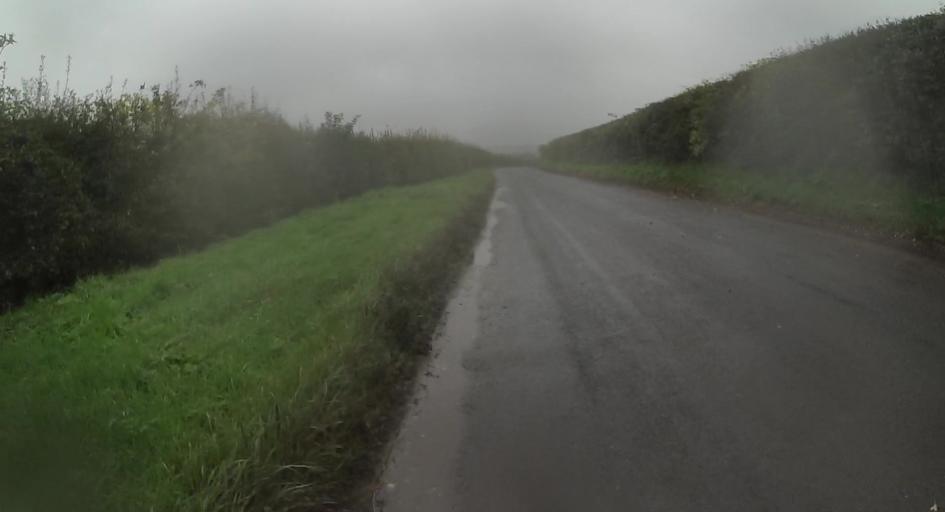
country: GB
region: England
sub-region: Hampshire
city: Four Marks
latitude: 51.1625
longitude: -1.1260
